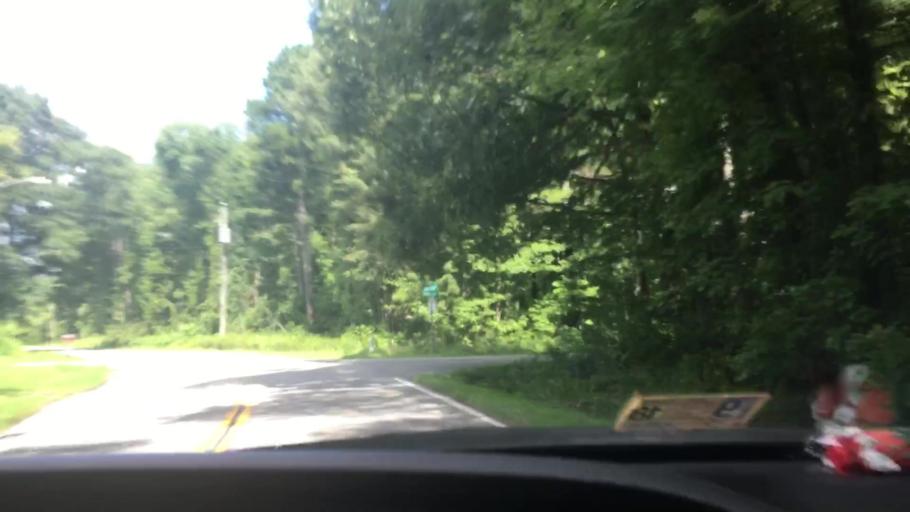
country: US
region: Virginia
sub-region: City of Virginia Beach
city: Virginia Beach
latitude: 36.7362
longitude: -76.1005
